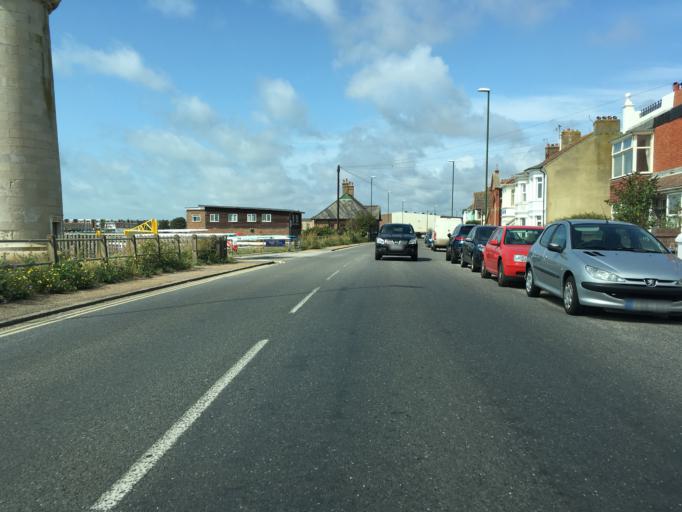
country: GB
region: England
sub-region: West Sussex
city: Shoreham-by-Sea
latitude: 50.8310
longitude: -0.2479
